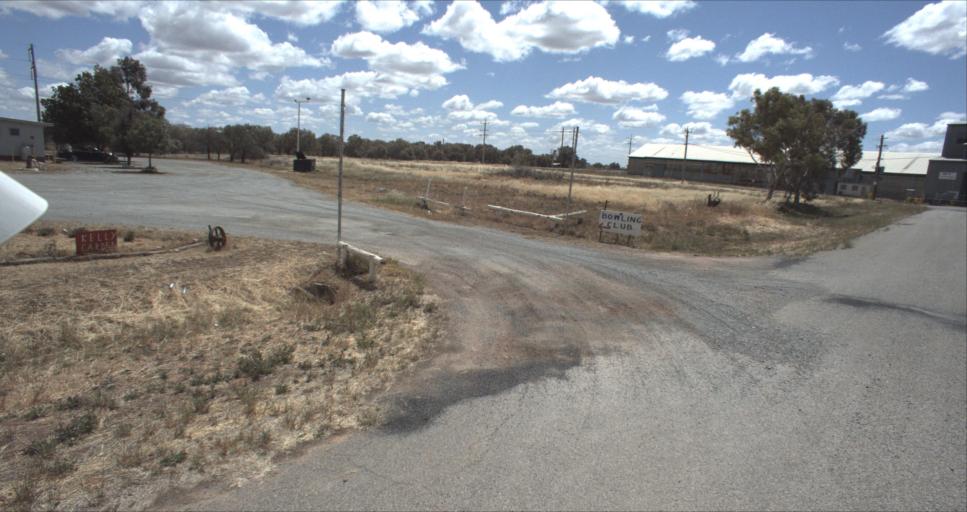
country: AU
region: New South Wales
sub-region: Murrumbidgee Shire
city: Darlington Point
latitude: -34.5161
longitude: 146.1778
